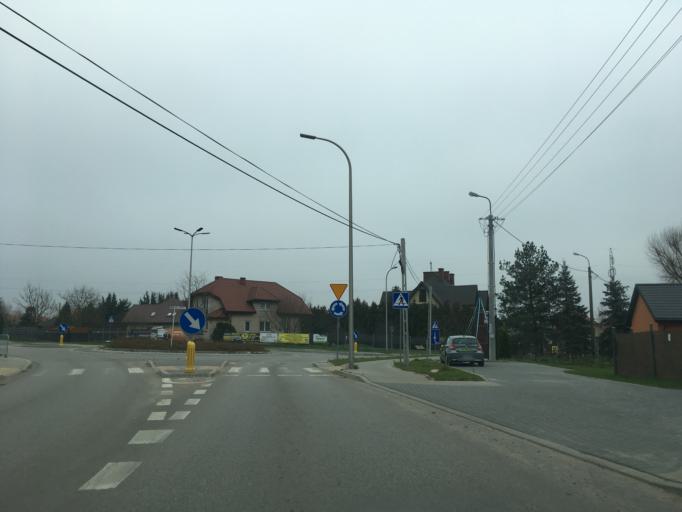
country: PL
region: Masovian Voivodeship
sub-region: Powiat piaseczynski
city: Lesznowola
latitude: 52.0495
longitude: 20.9318
